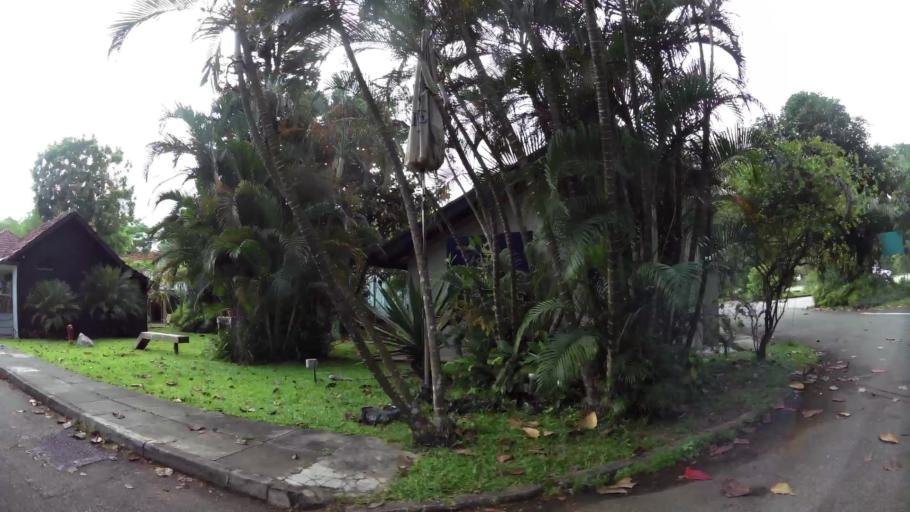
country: SG
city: Singapore
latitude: 1.3050
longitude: 103.8083
